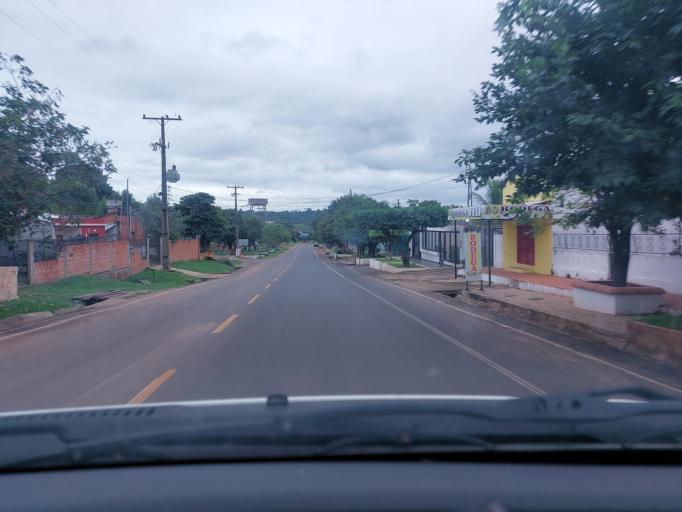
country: PY
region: San Pedro
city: Guayaybi
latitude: -24.6603
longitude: -56.4396
